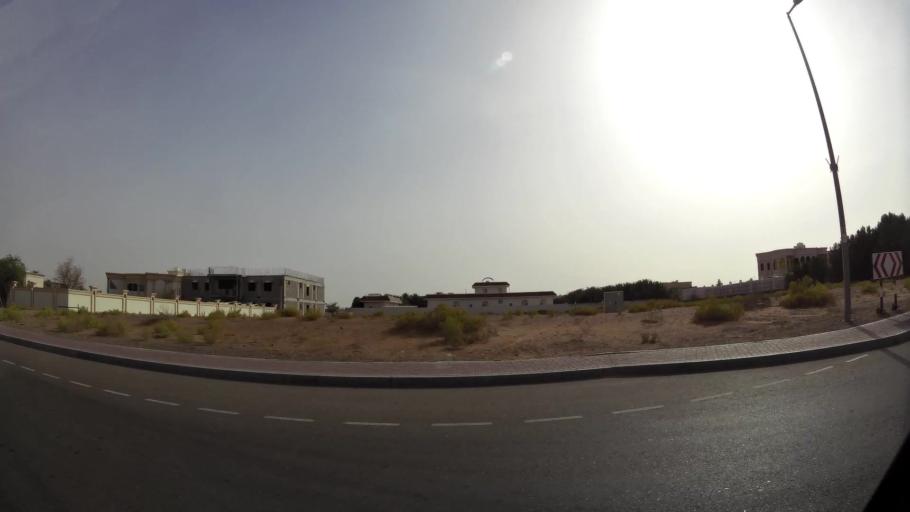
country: AE
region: Abu Dhabi
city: Al Ain
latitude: 24.2023
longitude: 55.6144
